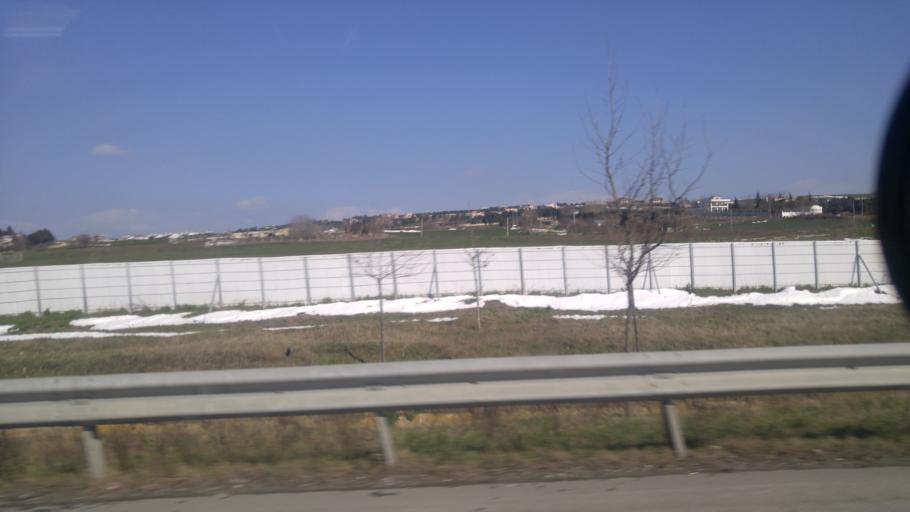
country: TR
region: Istanbul
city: Selimpasa
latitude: 41.0734
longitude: 28.3788
